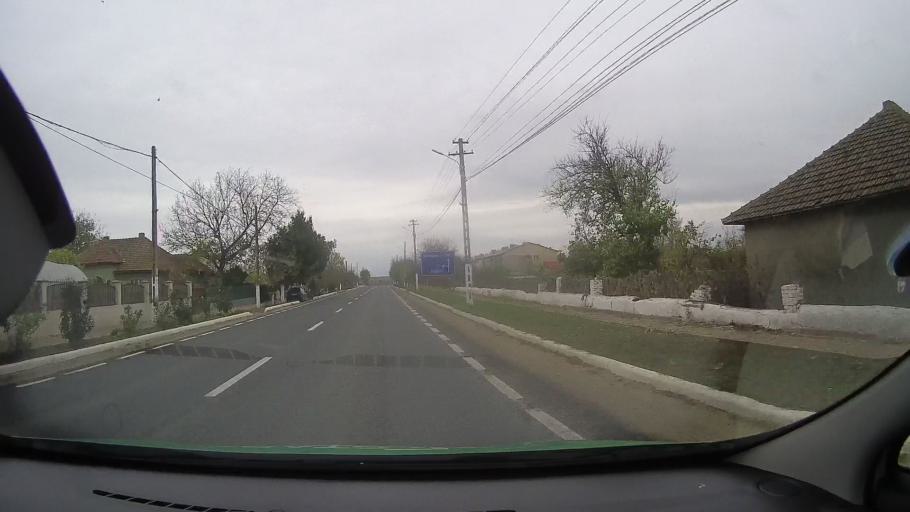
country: RO
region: Constanta
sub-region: Comuna Nicolae Balcescu
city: Nicolae Balcescu
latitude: 44.3876
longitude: 28.3842
